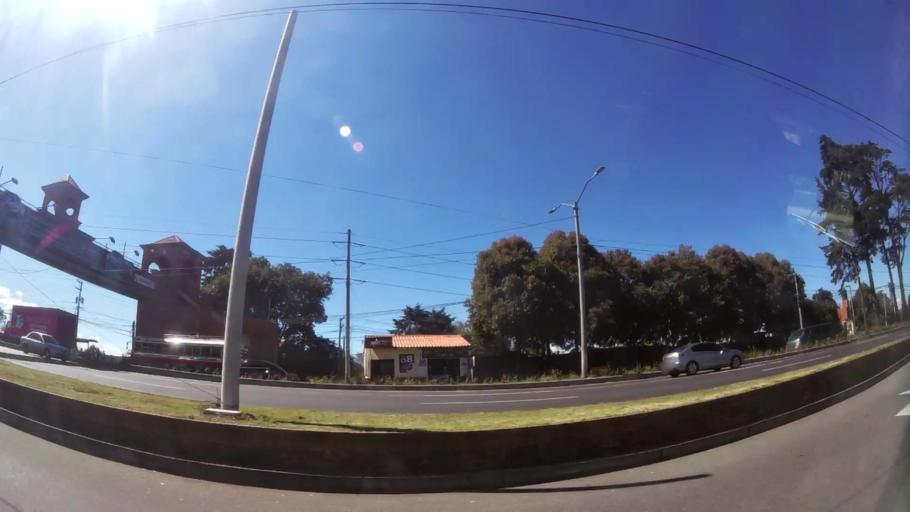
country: GT
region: Guatemala
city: Santa Catarina Pinula
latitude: 14.5517
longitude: -90.4549
